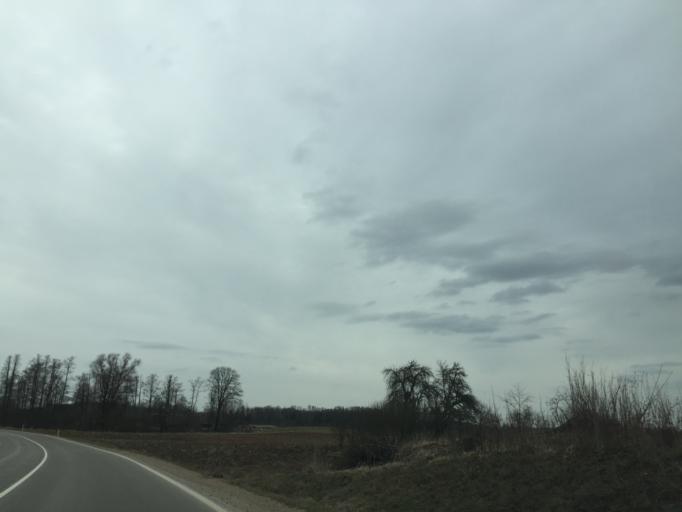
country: LV
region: Ilukste
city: Ilukste
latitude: 55.9985
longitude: 26.2846
